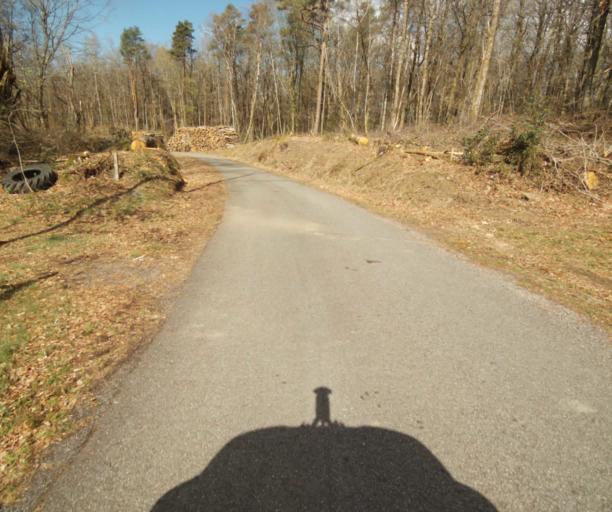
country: FR
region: Limousin
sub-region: Departement de la Correze
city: Argentat
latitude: 45.2315
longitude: 1.9210
